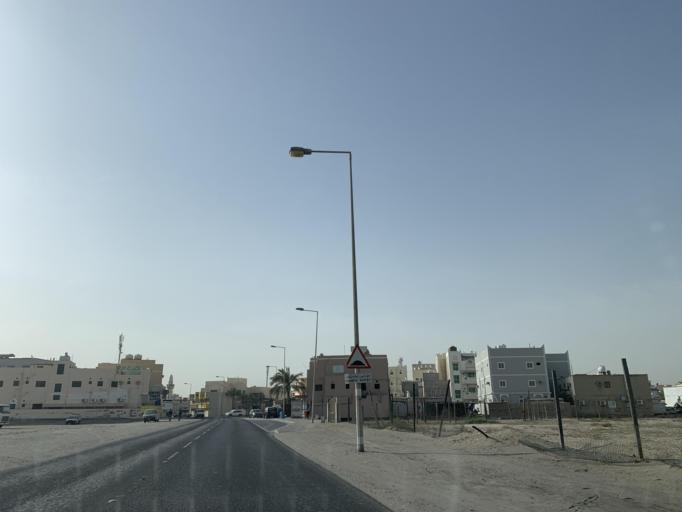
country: BH
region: Northern
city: Madinat `Isa
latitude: 26.1812
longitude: 50.5602
